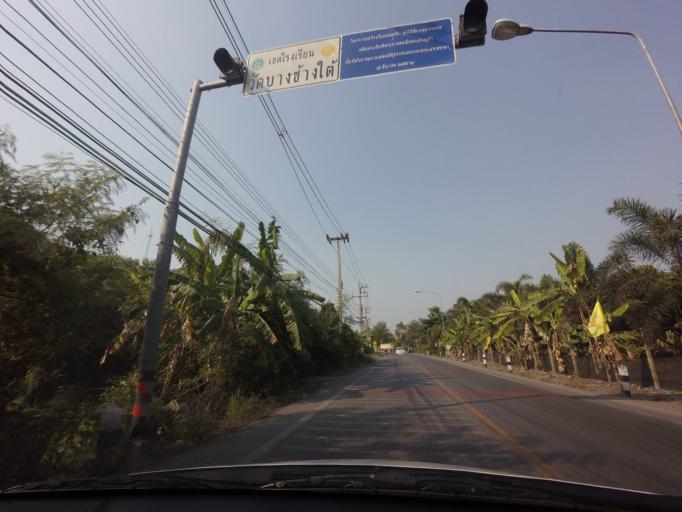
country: TH
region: Nakhon Pathom
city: Sam Phran
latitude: 13.7122
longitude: 100.2068
